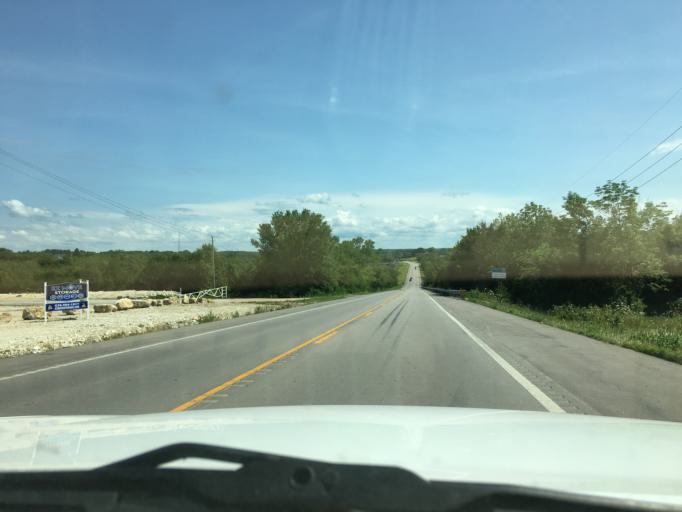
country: US
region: Missouri
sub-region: Franklin County
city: Union
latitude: 38.4696
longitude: -91.0057
